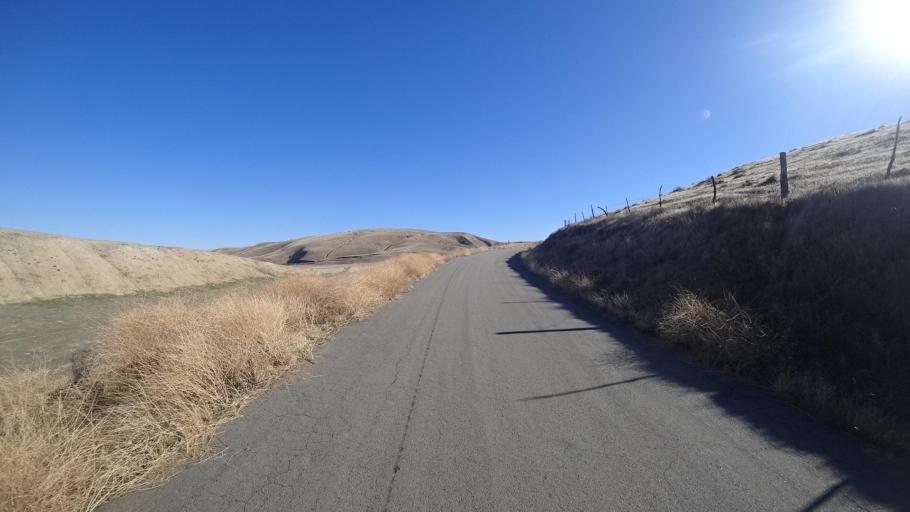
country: US
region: California
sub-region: Kern County
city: Maricopa
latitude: 34.9667
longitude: -119.4497
